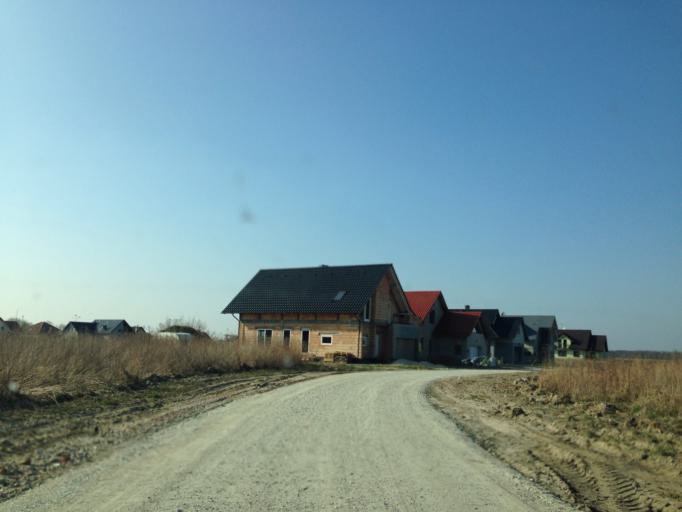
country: PL
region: Lower Silesian Voivodeship
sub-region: Powiat wroclawski
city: Kamieniec Wroclawski
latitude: 51.0997
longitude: 17.2115
